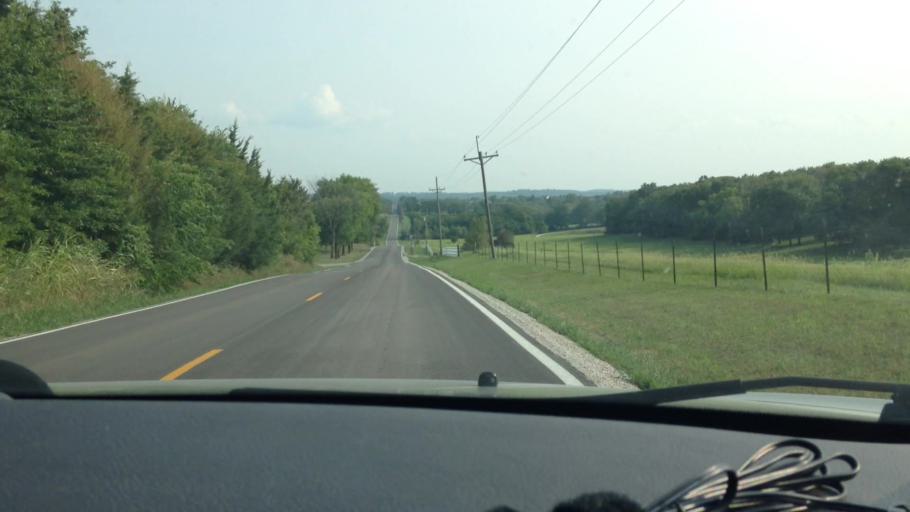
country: US
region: Missouri
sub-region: Platte County
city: Platte City
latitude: 39.4175
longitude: -94.7798
